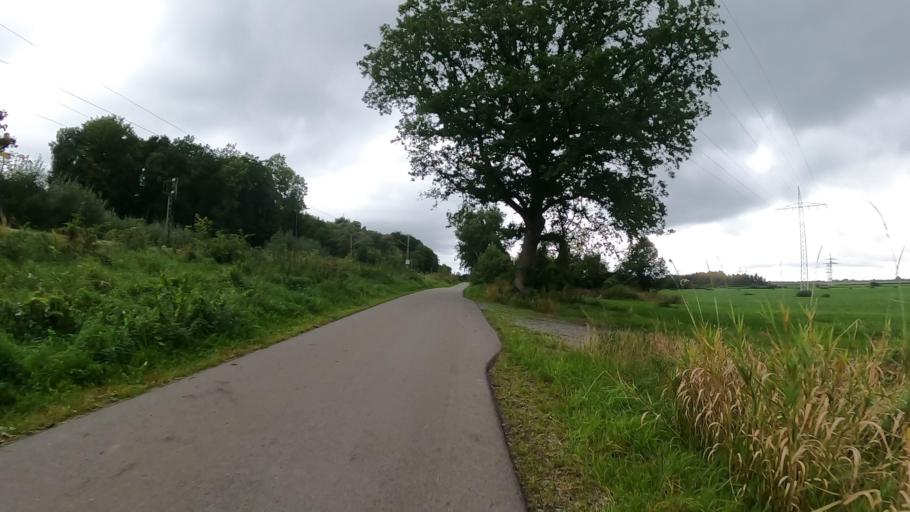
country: DE
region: Lower Saxony
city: Agathenburg
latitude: 53.5577
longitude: 9.5437
